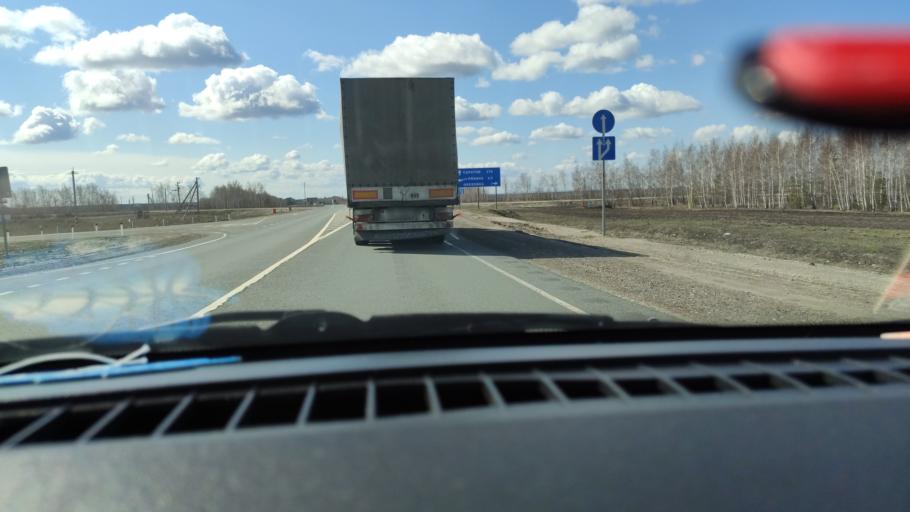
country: RU
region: Samara
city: Syzran'
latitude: 52.9233
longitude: 48.3033
